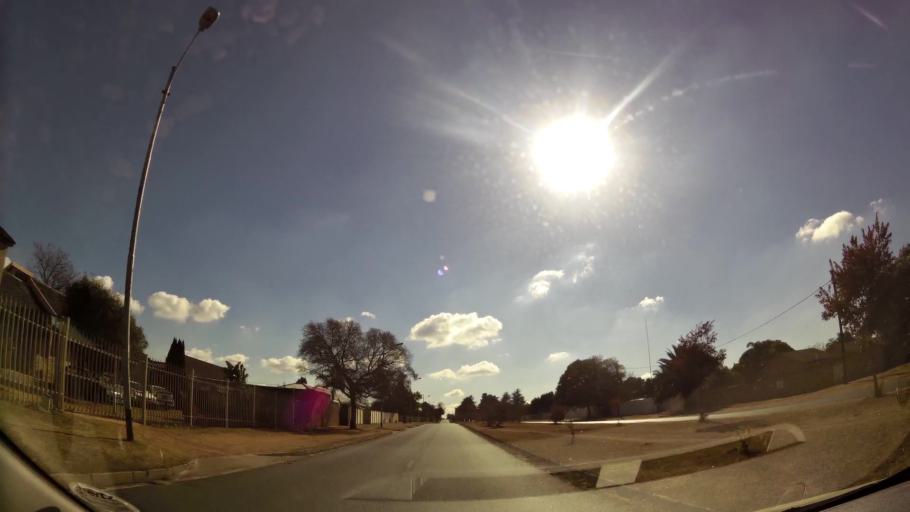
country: ZA
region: Gauteng
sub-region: City of Johannesburg Metropolitan Municipality
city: Roodepoort
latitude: -26.1435
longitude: 27.8349
